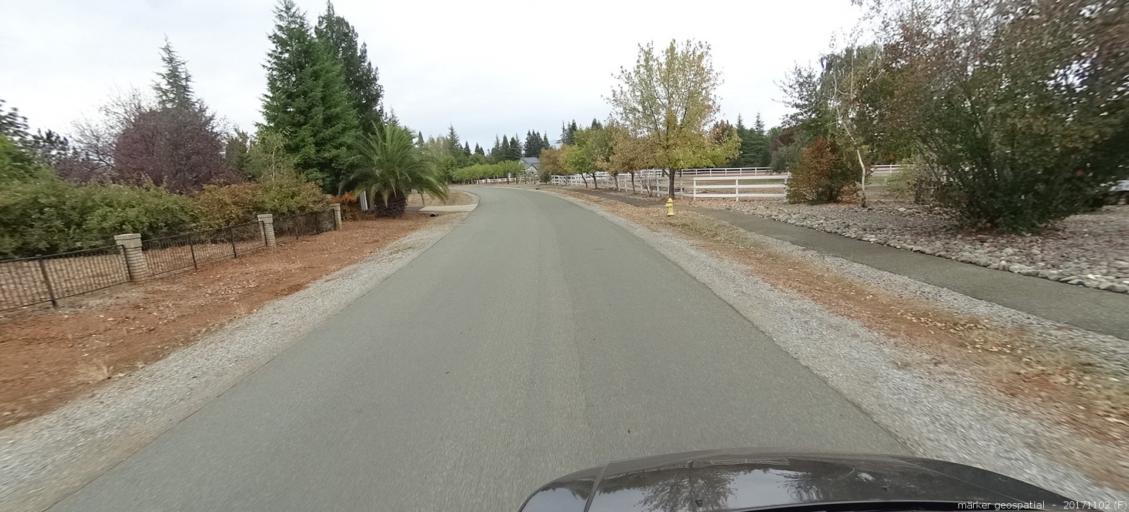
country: US
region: California
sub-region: Shasta County
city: Shasta Lake
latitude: 40.6544
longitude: -122.3231
